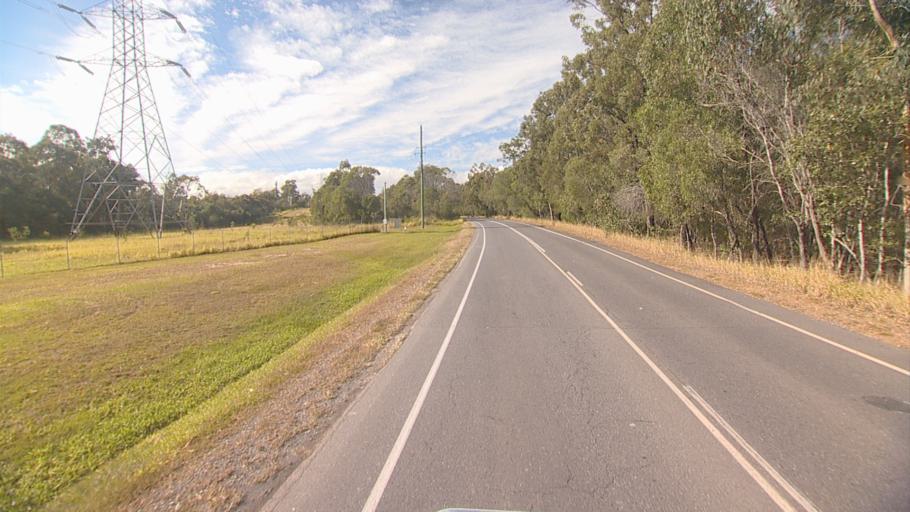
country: AU
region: Queensland
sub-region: Brisbane
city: Forest Lake
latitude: -27.6320
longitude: 152.9477
